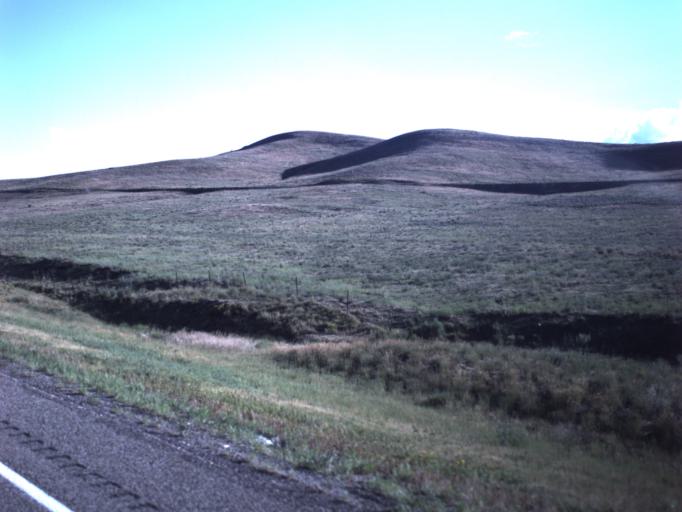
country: US
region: Utah
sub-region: Sanpete County
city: Fairview
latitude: 39.7390
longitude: -111.4772
